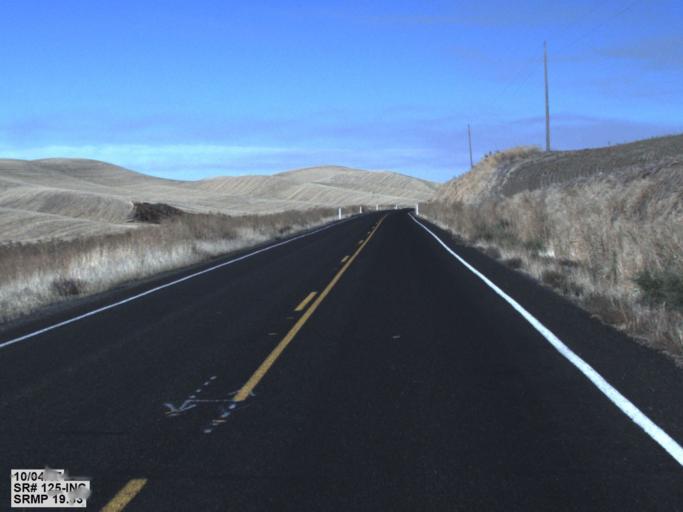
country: US
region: Washington
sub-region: Walla Walla County
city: Walla Walla
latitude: 46.2401
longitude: -118.3679
